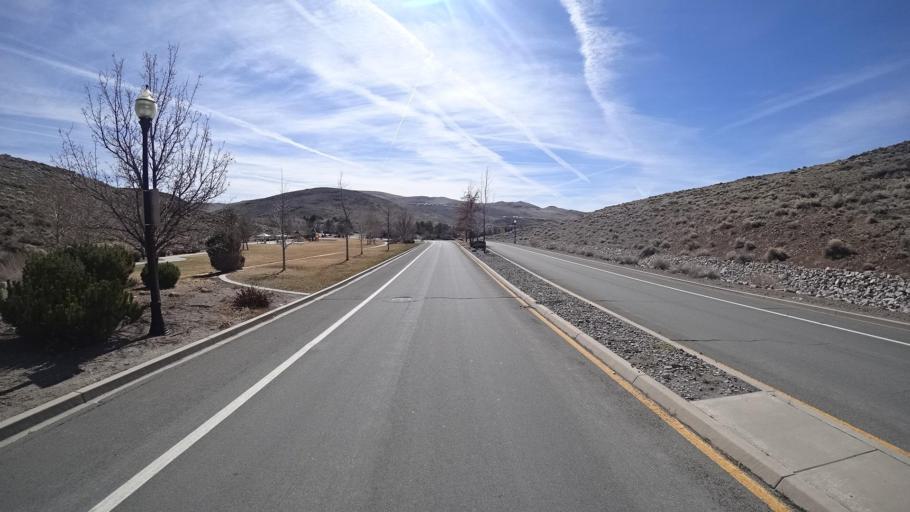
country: US
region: Nevada
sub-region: Washoe County
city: Sparks
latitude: 39.5742
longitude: -119.6958
